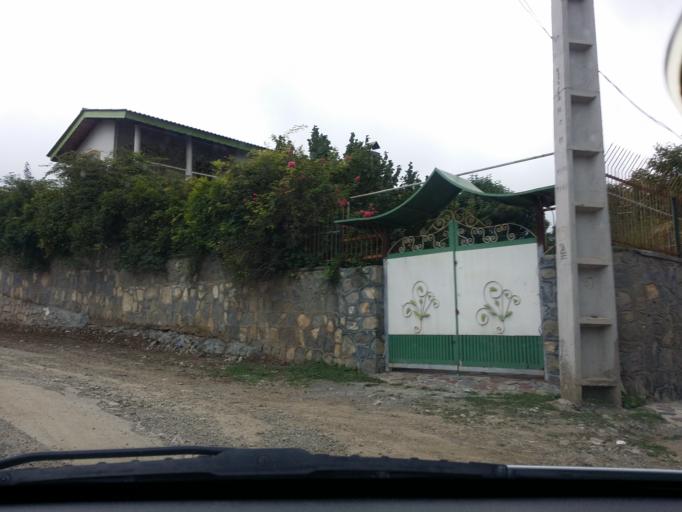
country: IR
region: Mazandaran
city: `Abbasabad
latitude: 36.4897
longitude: 51.1367
